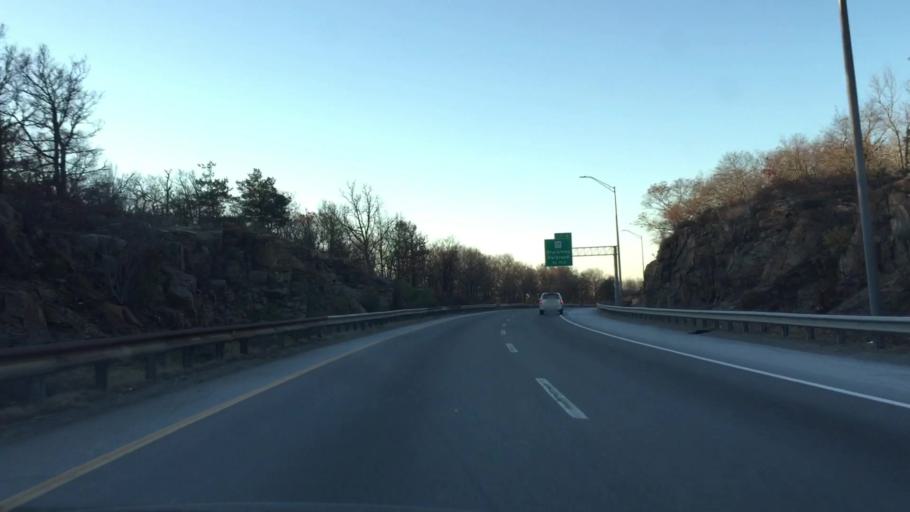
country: US
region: Massachusetts
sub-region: Norfolk County
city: Braintree
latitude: 42.2286
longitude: -71.0236
